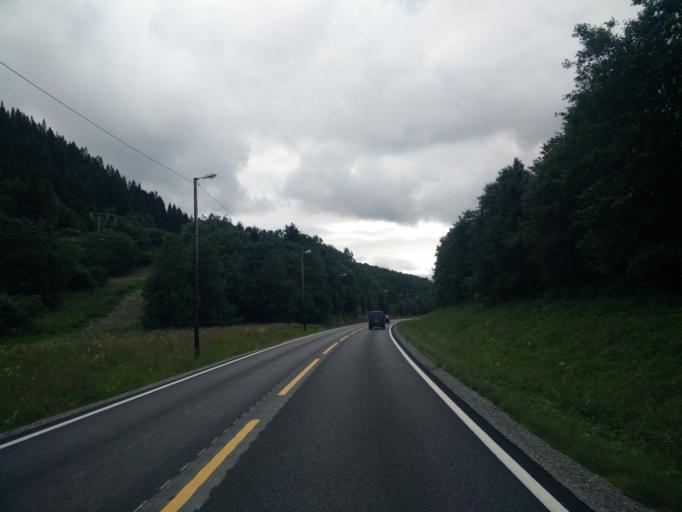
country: NO
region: Sor-Trondelag
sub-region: Orkdal
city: Orkanger
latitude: 63.2814
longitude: 9.8467
